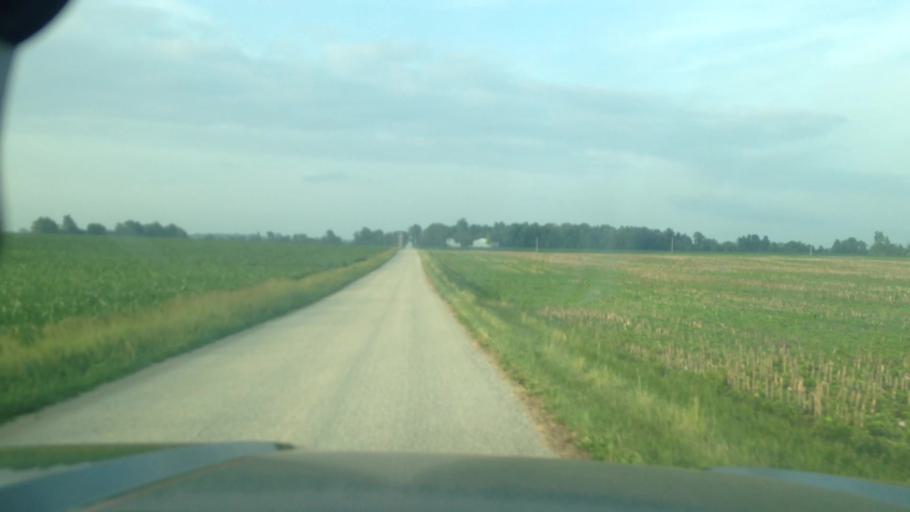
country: US
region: Indiana
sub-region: Randolph County
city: Union City
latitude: 40.2487
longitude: -84.8625
